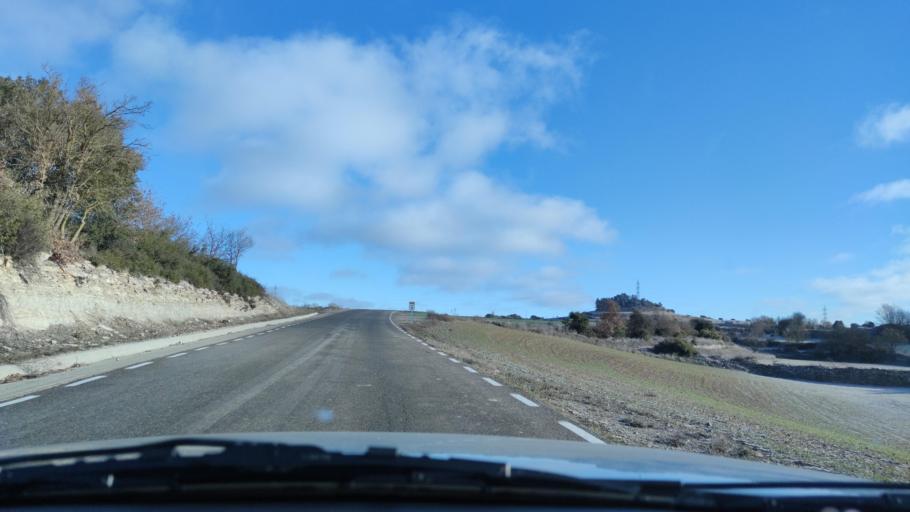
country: ES
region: Catalonia
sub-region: Provincia de Barcelona
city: Pujalt
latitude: 41.7128
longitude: 1.3547
